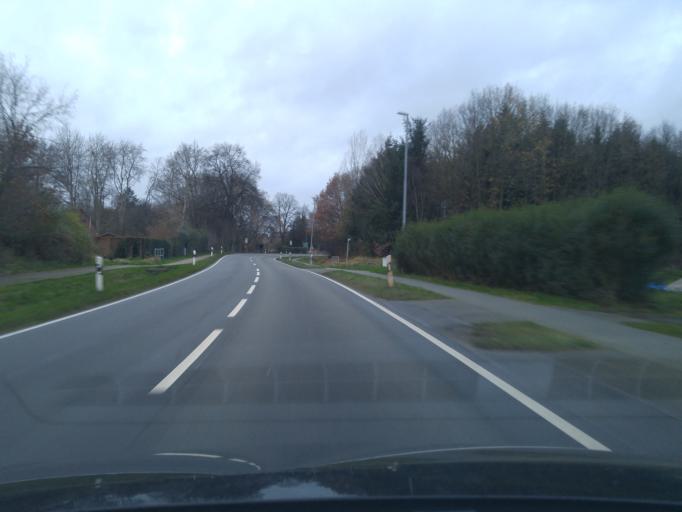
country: DE
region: Schleswig-Holstein
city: Lauenburg
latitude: 53.3531
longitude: 10.5643
